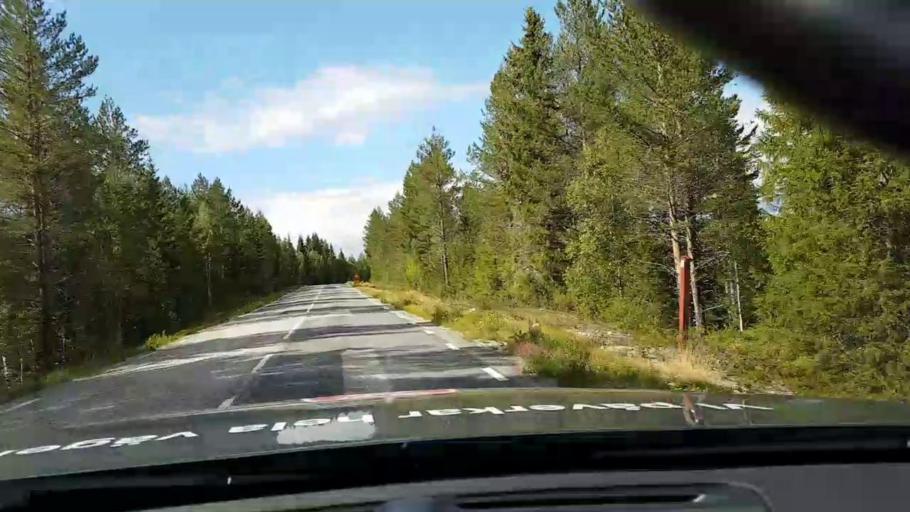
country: SE
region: Vaesterbotten
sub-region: Asele Kommun
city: Asele
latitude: 63.8153
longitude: 17.5015
